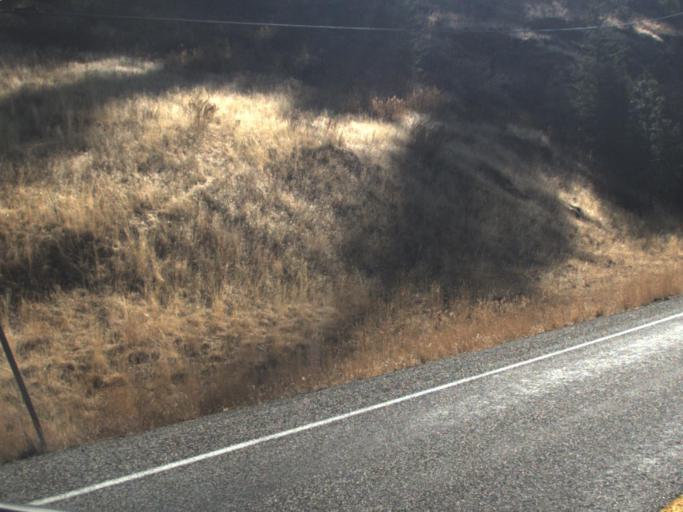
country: US
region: Washington
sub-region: Ferry County
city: Republic
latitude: 48.6709
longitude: -118.6672
